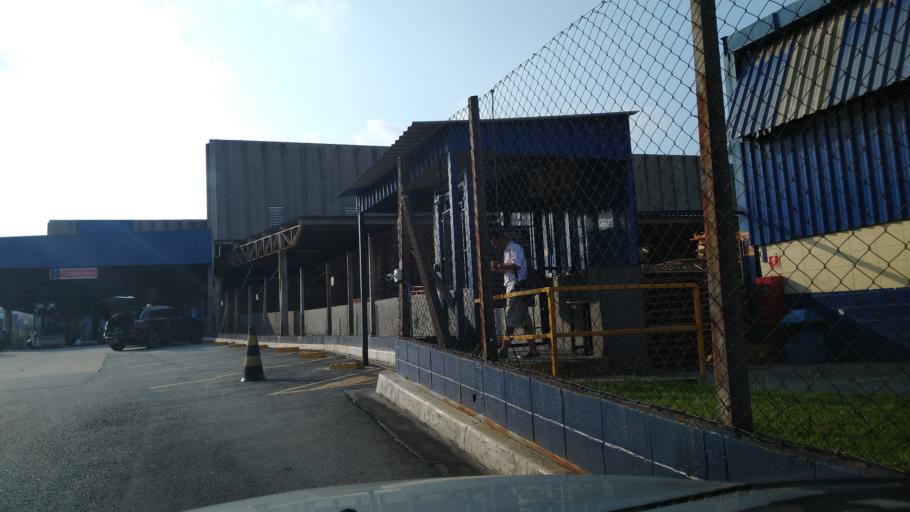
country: BR
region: Sao Paulo
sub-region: Guarulhos
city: Guarulhos
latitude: -23.4902
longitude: -46.5423
